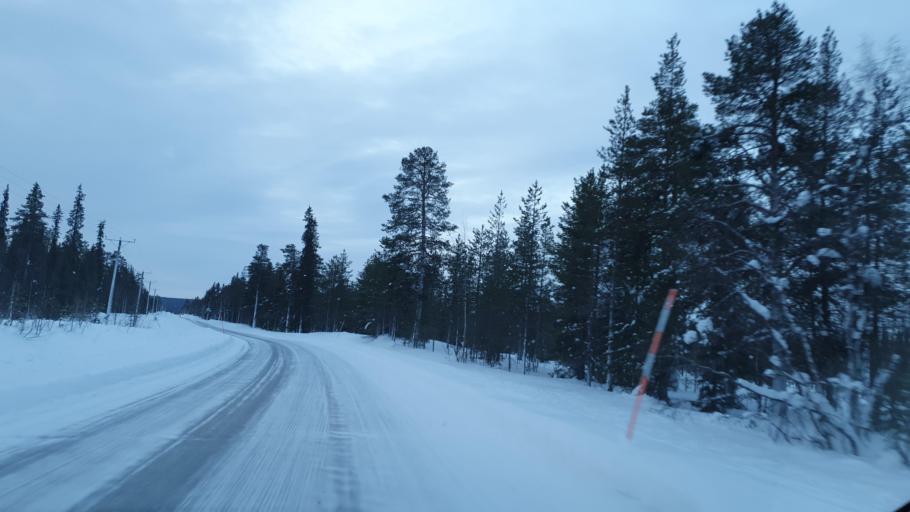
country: FI
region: Lapland
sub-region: Tunturi-Lappi
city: Kolari
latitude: 67.6305
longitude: 24.1568
